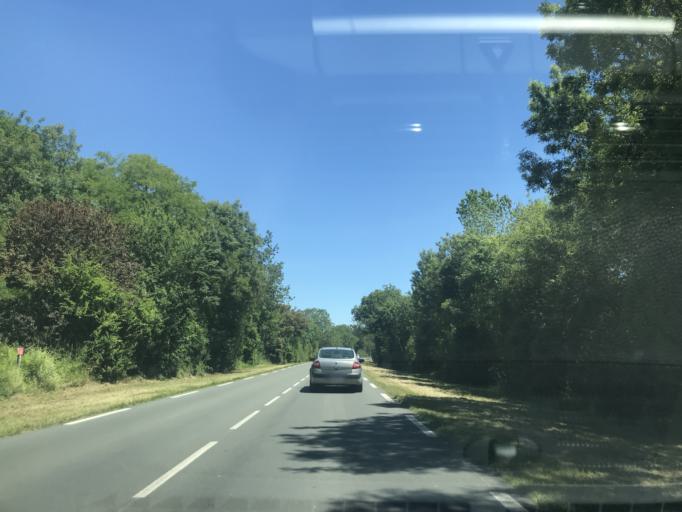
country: FR
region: Poitou-Charentes
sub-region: Departement de la Charente-Maritime
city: Meschers-sur-Gironde
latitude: 45.5640
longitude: -0.9503
